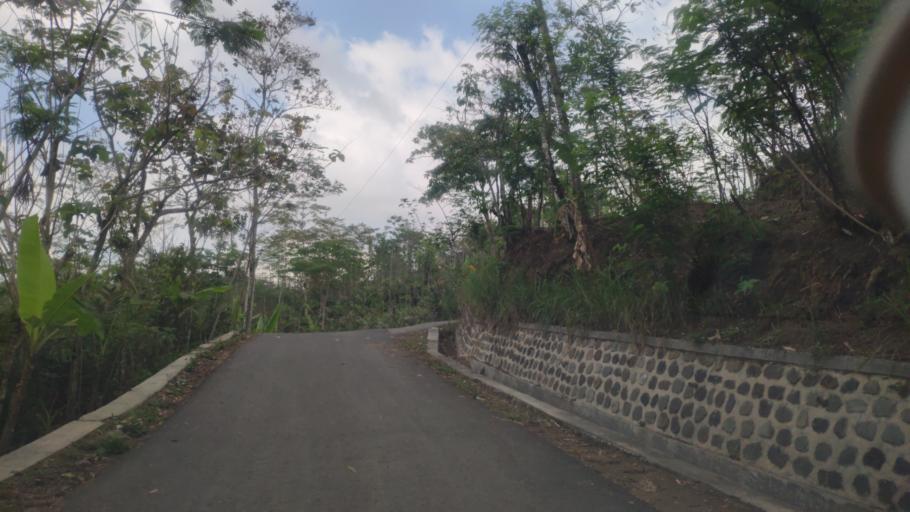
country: ID
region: Central Java
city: Wonosobo
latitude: -7.3130
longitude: 109.7613
